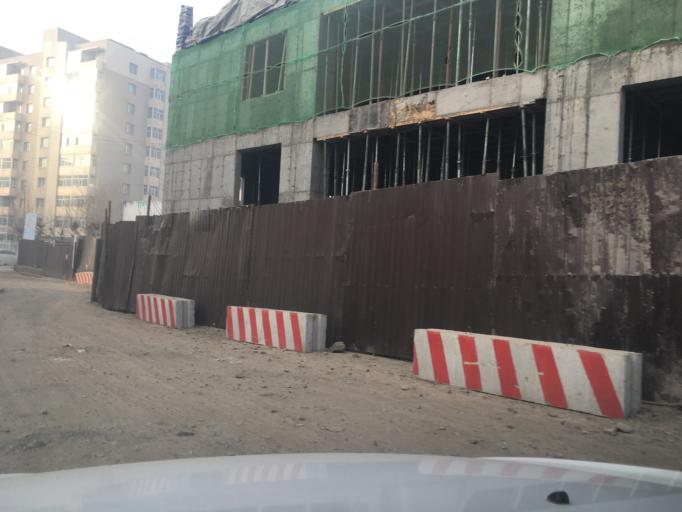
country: MN
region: Ulaanbaatar
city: Ulaanbaatar
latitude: 47.9172
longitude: 106.8677
